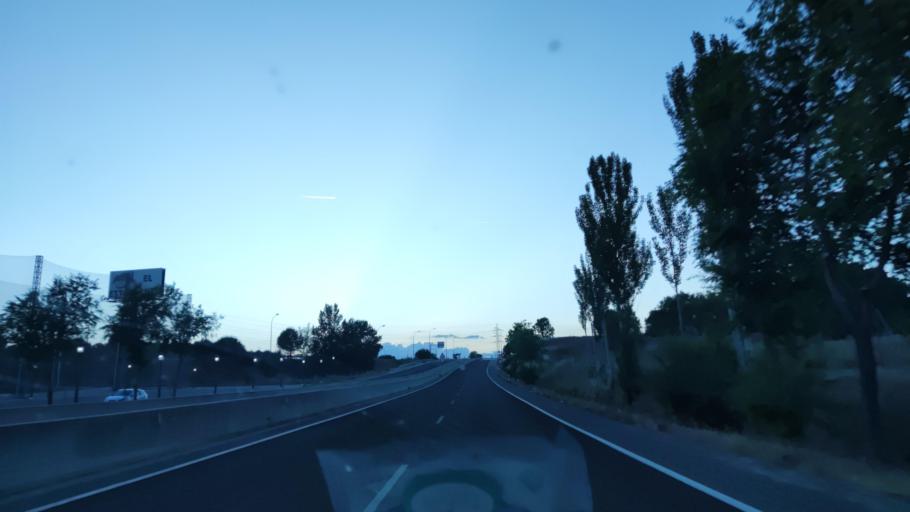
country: ES
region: Madrid
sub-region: Provincia de Madrid
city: San Sebastian de los Reyes
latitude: 40.5217
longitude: -3.5945
